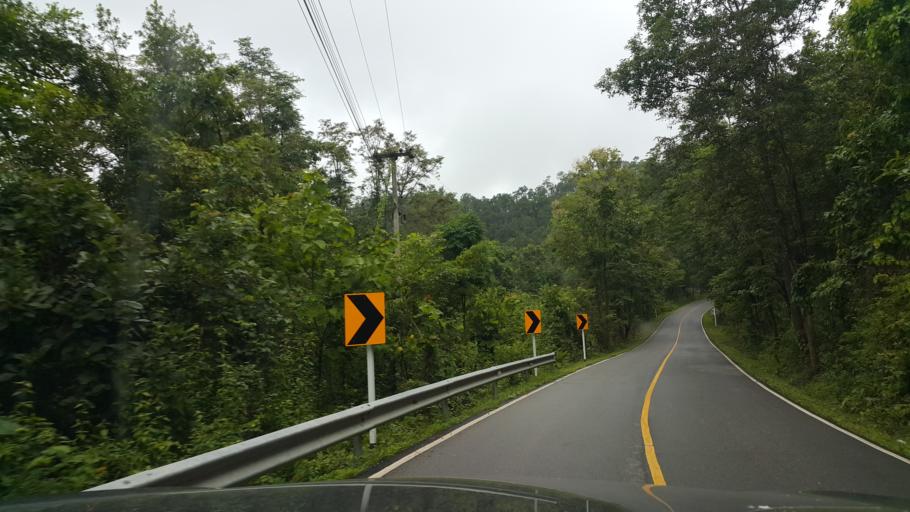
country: TH
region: Chiang Mai
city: Samoeng
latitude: 18.8601
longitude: 98.6701
